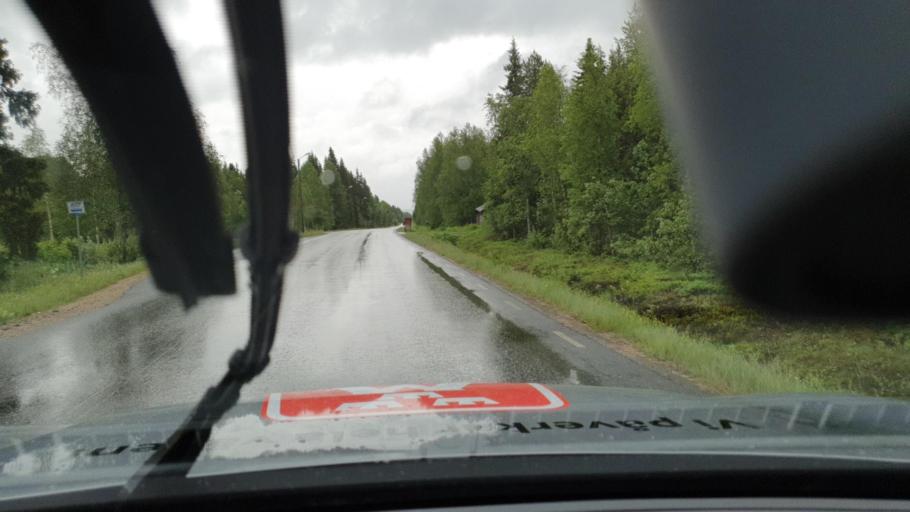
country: FI
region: Lapland
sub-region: Torniolaakso
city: Ylitornio
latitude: 66.2498
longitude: 23.6690
